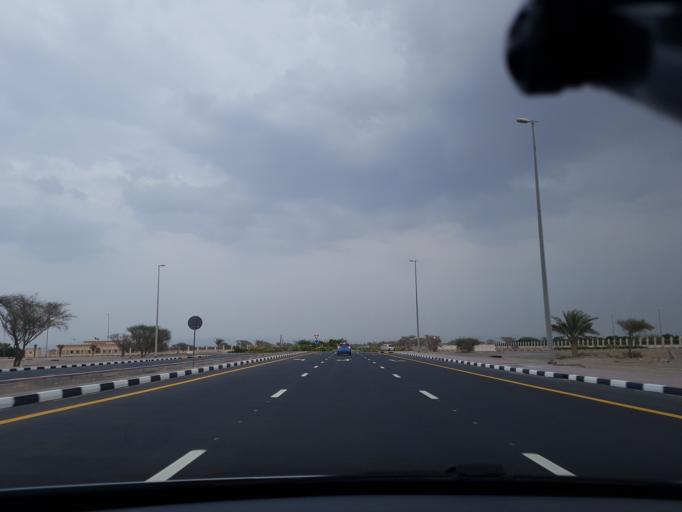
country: AE
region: Ash Shariqah
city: Adh Dhayd
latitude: 25.2675
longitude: 55.9098
